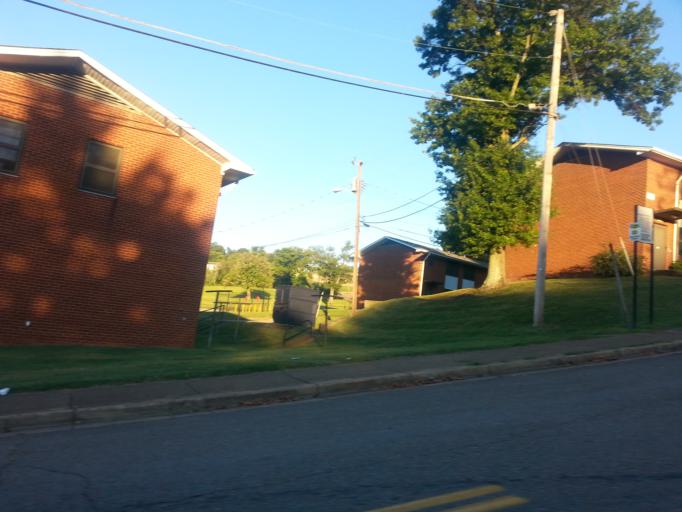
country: US
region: Tennessee
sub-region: Knox County
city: Knoxville
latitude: 35.9712
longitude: -83.9088
